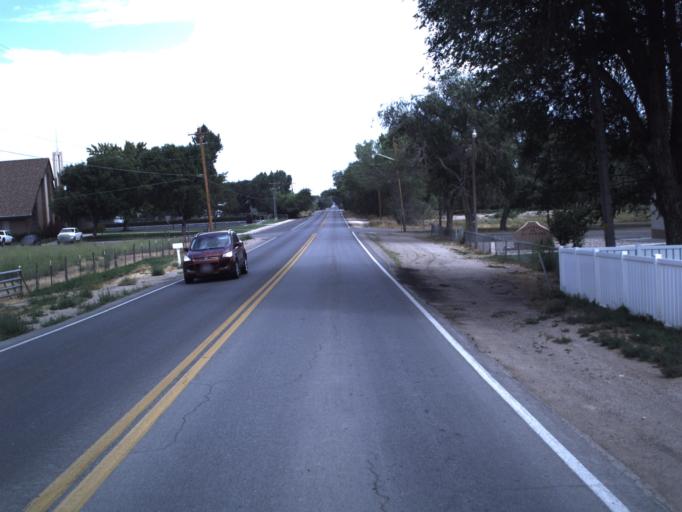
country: US
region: Utah
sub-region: Uintah County
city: Naples
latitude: 40.3967
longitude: -109.4989
